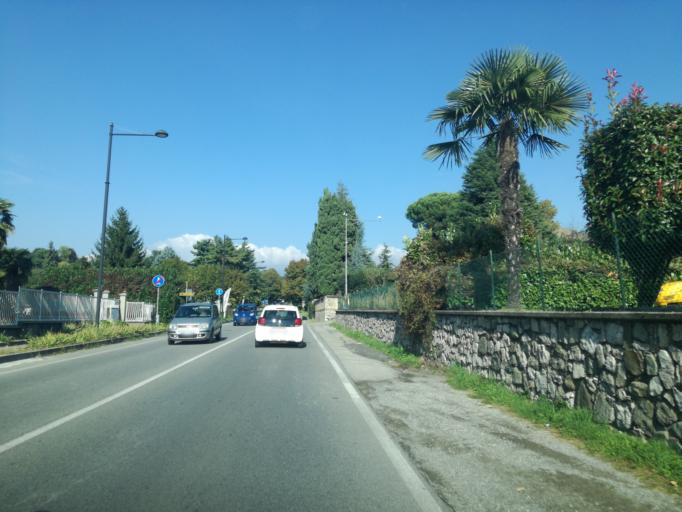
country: IT
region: Lombardy
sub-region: Provincia di Lecco
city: Robbiate
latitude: 45.6913
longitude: 9.4365
